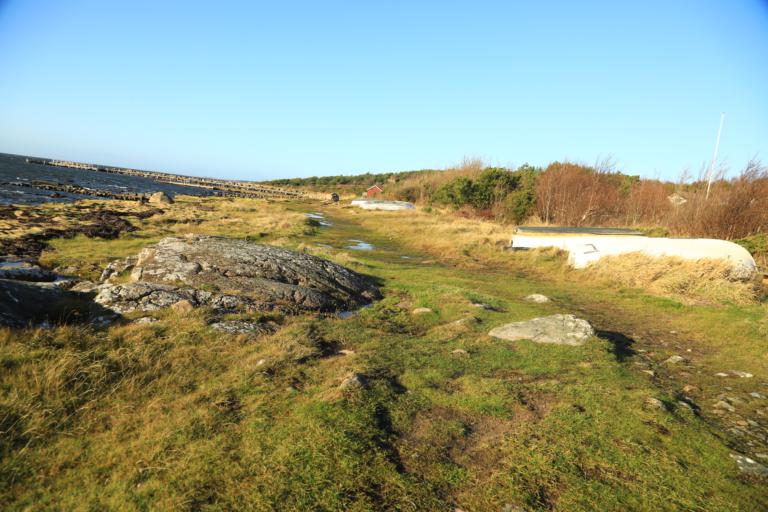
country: SE
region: Halland
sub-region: Varbergs Kommun
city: Varberg
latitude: 57.1678
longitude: 12.2122
